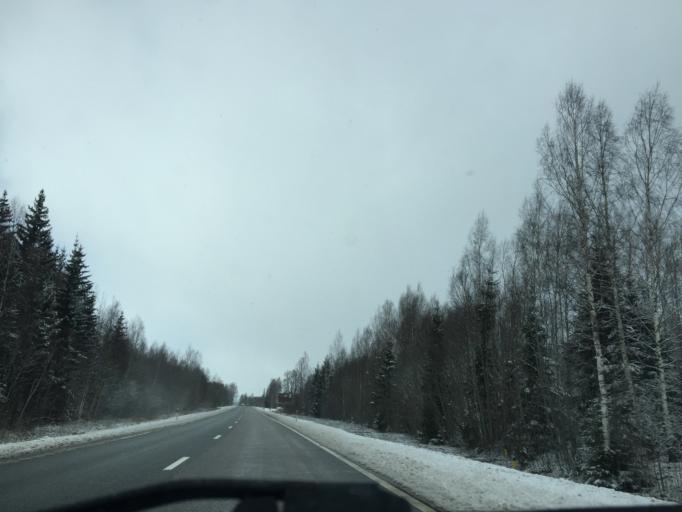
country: LV
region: Kandava
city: Kandava
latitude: 57.0925
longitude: 22.7969
